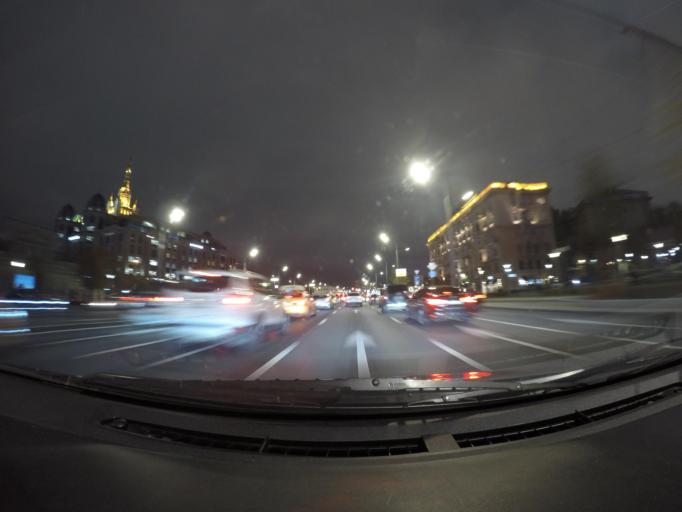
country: RU
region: Moskovskaya
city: Dorogomilovo
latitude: 55.7567
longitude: 37.5843
